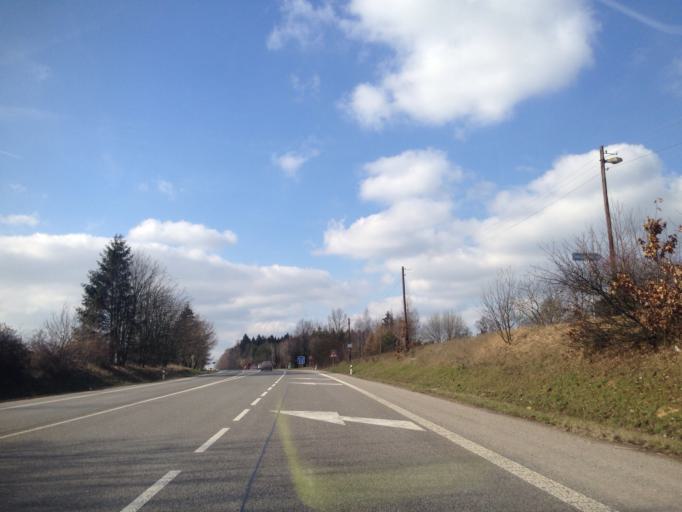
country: CZ
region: Kralovehradecky
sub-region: Okres Jicin
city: Sobotka
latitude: 50.4583
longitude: 15.2159
